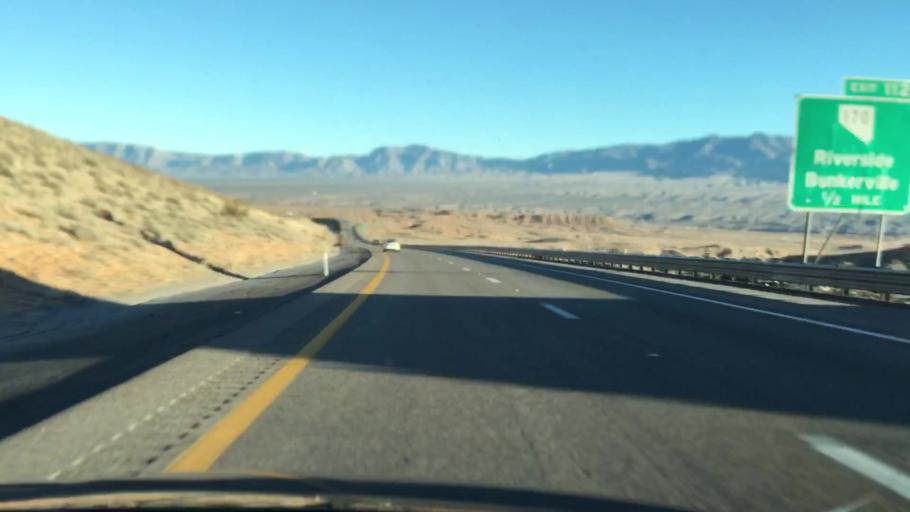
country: US
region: Nevada
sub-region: Clark County
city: Bunkerville
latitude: 36.7747
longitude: -114.2494
